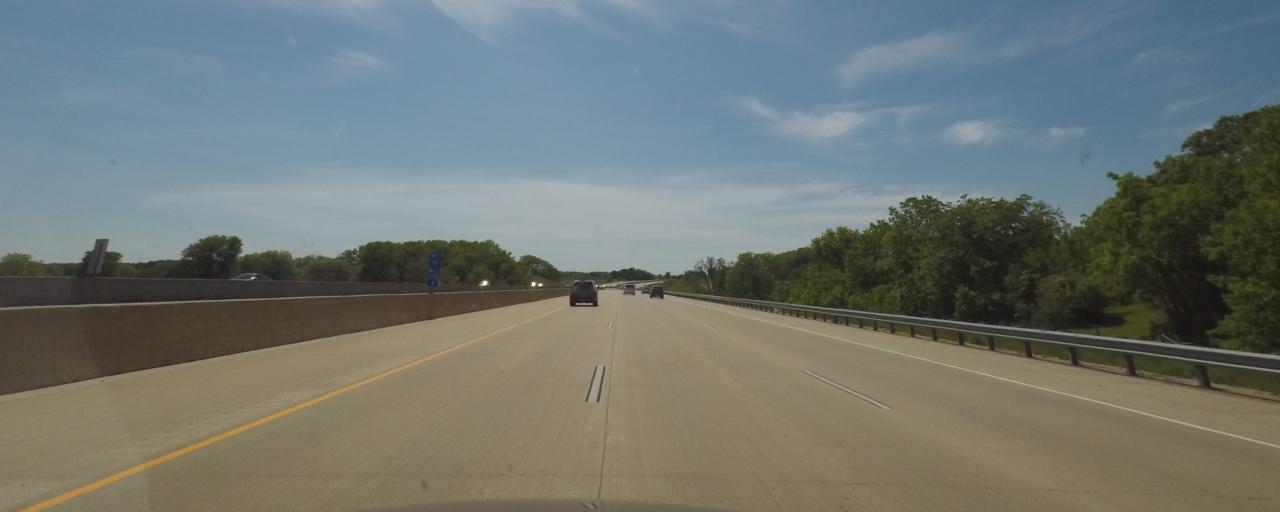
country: US
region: Wisconsin
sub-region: Dane County
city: Cottage Grove
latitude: 43.1058
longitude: -89.2423
